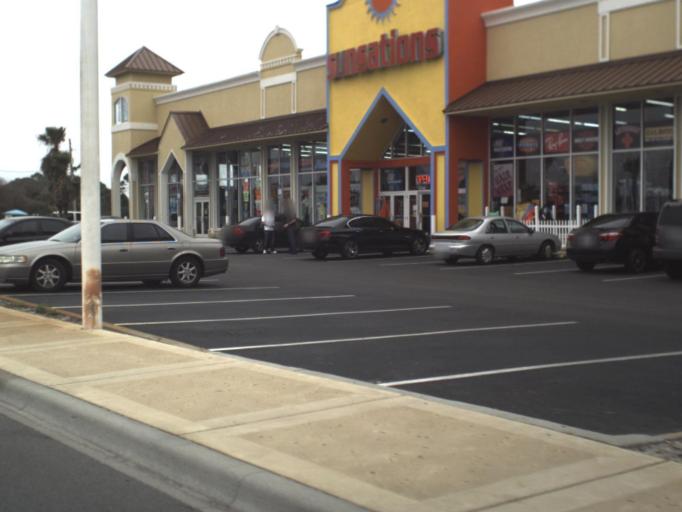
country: US
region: Florida
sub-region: Bay County
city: Panama City Beach
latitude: 30.1779
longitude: -85.8035
